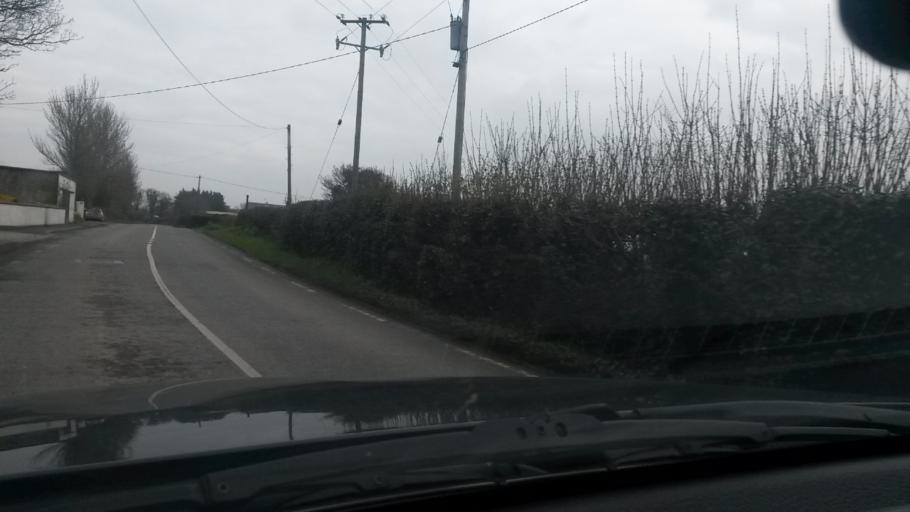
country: IE
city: Bonnybrook
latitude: 53.4141
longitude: -6.2140
